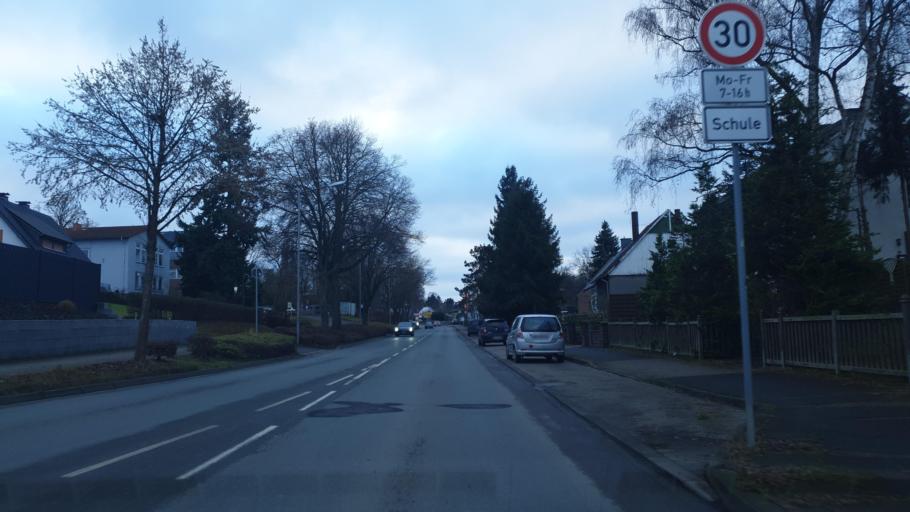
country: DE
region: North Rhine-Westphalia
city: Loehne
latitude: 52.1869
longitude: 8.6893
